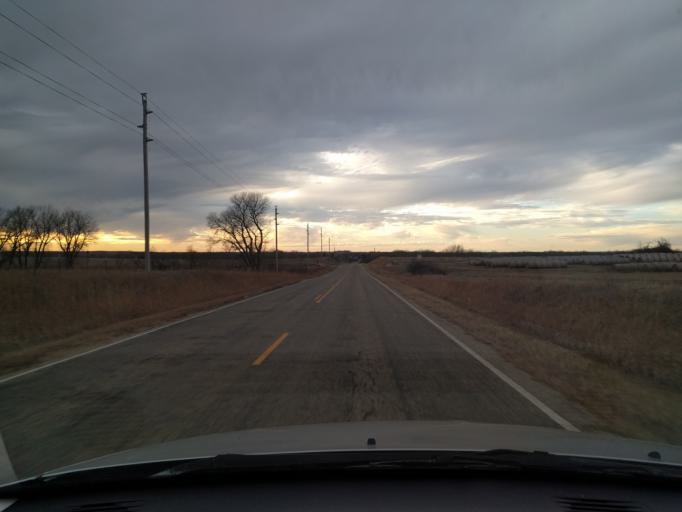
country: US
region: Kansas
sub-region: Clay County
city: Clay Center
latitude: 39.2488
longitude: -97.3227
